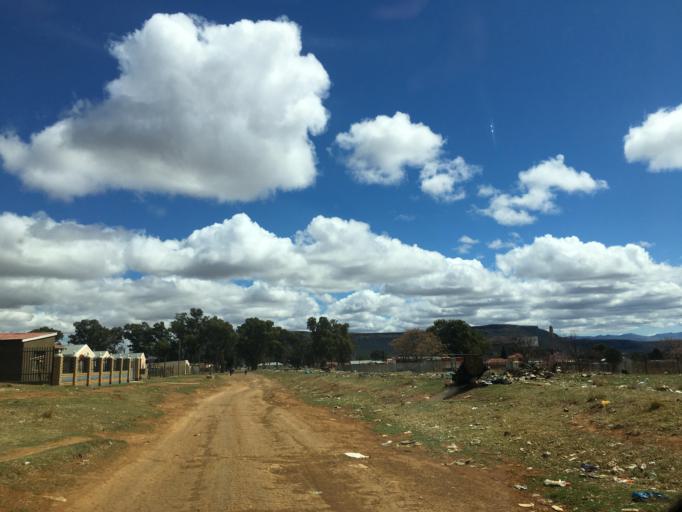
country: ZA
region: Eastern Cape
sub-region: Chris Hani District Municipality
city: Cala
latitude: -31.5302
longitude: 27.7057
